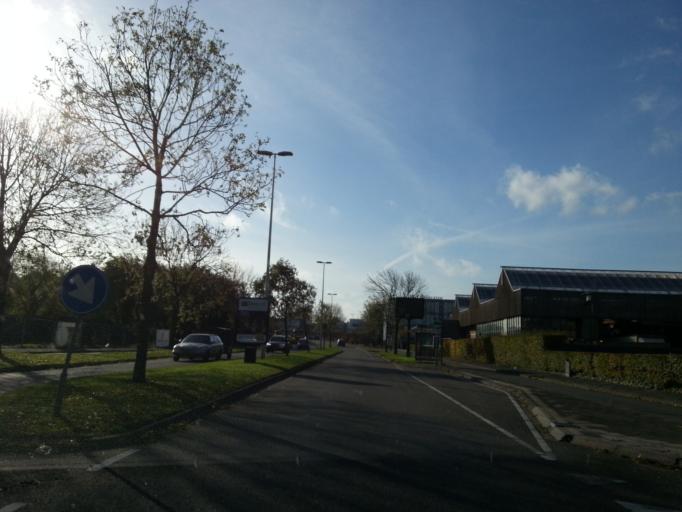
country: NL
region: South Holland
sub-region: Gemeente Leiden
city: Leiden
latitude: 52.1569
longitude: 4.4732
